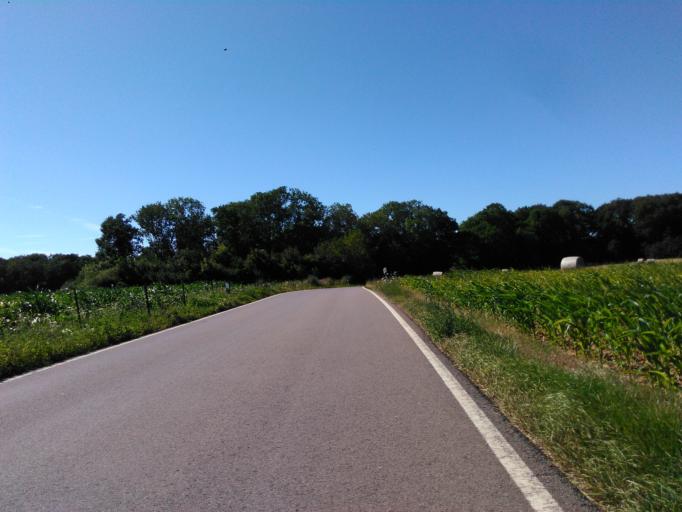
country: LU
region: Luxembourg
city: Schouweiler
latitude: 49.5678
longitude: 5.9714
